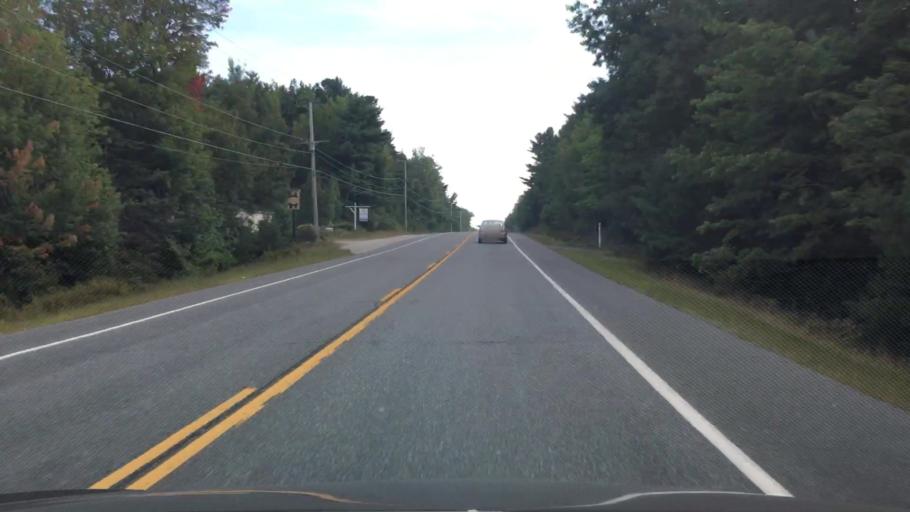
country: US
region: Maine
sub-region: Hancock County
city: Surry
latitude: 44.4480
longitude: -68.5600
